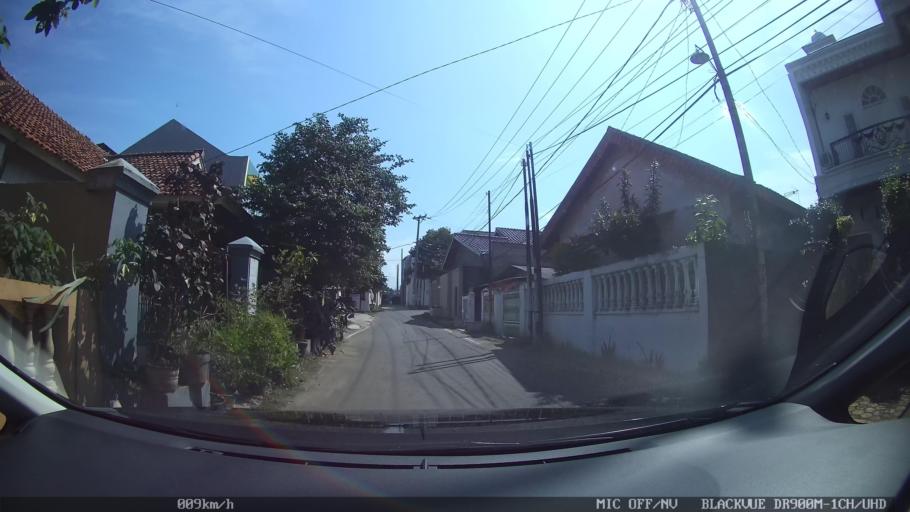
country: ID
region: Lampung
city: Kedaton
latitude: -5.3728
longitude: 105.2453
